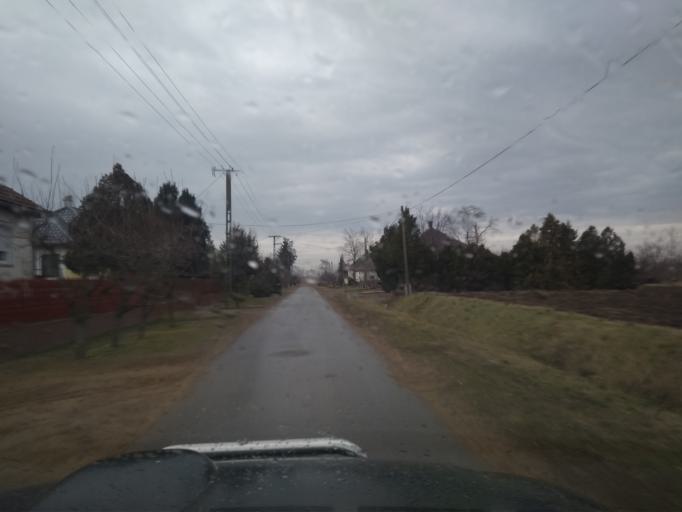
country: HU
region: Szabolcs-Szatmar-Bereg
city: Apagy
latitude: 47.9665
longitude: 21.9244
